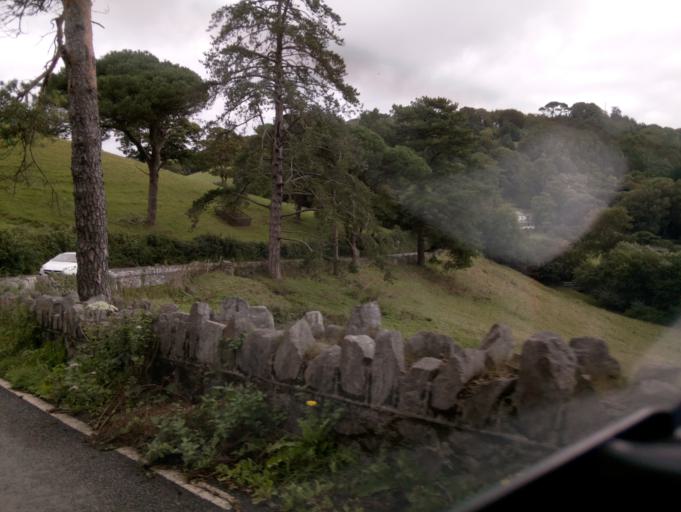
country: GB
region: England
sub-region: Devon
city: Dartmouth
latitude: 50.3183
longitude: -3.6147
